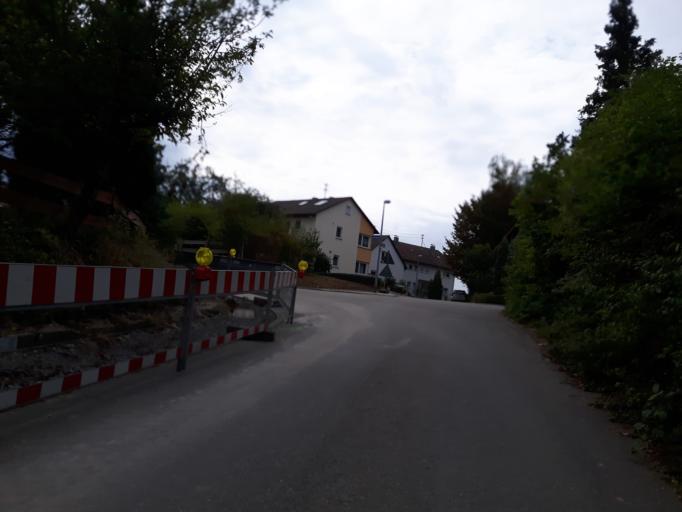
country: DE
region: Baden-Wuerttemberg
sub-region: Regierungsbezirk Stuttgart
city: Gemmingen
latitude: 49.1120
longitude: 8.9828
